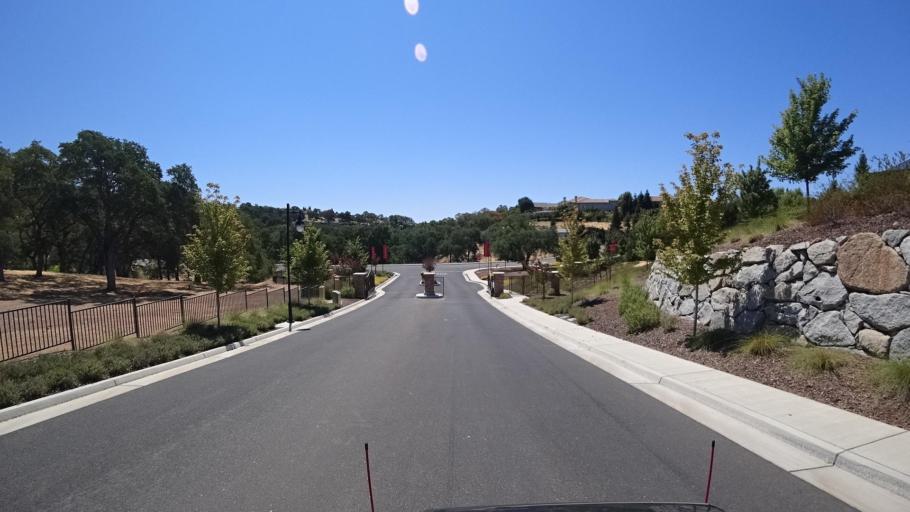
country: US
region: California
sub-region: Placer County
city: Rocklin
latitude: 38.8333
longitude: -121.2506
